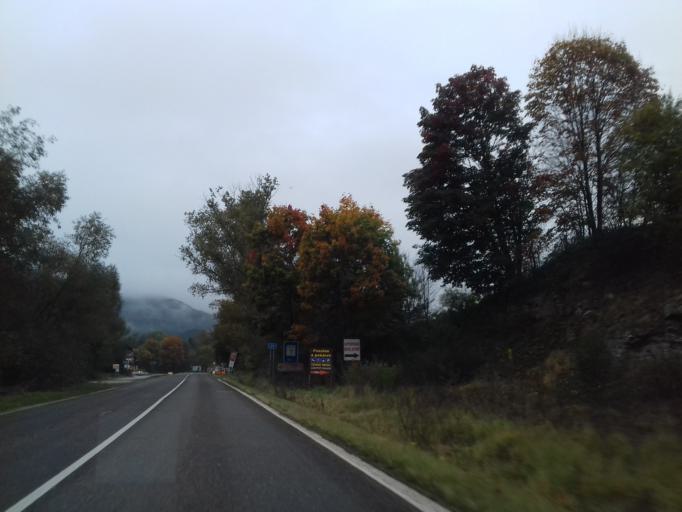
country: SK
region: Zilinsky
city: Ruzomberok
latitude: 48.9402
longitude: 19.2633
